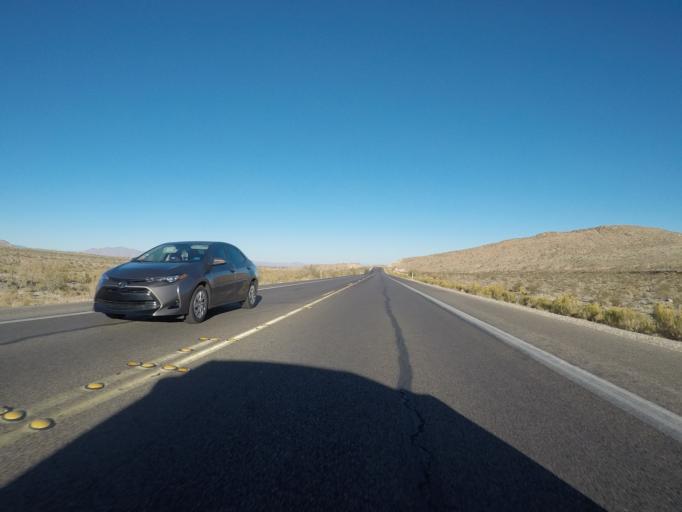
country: US
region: Nevada
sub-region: Clark County
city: Summerlin South
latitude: 36.1468
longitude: -115.3818
